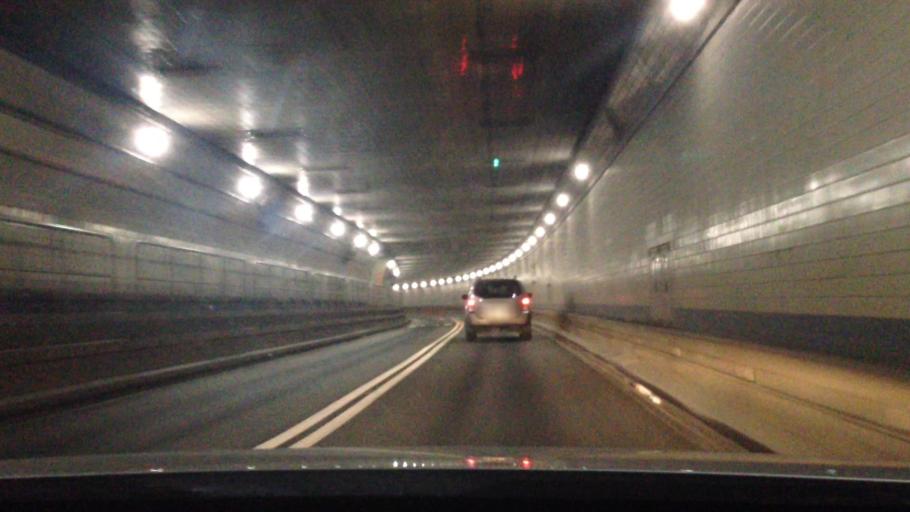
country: US
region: New Jersey
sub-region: Hudson County
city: Weehawken
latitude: 40.7647
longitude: -74.0177
